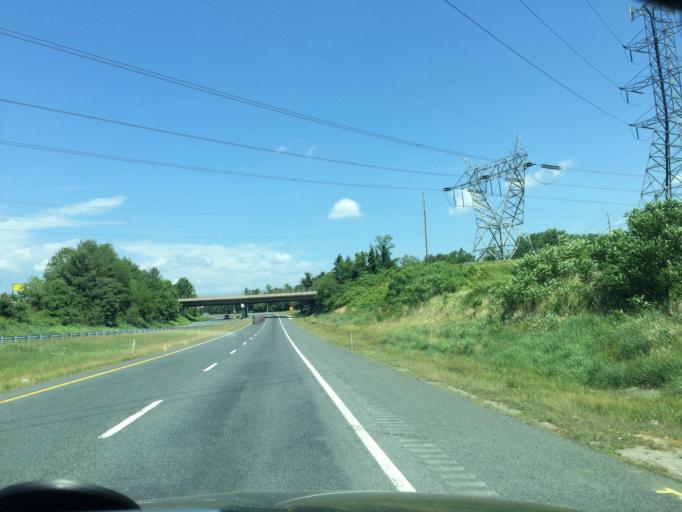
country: US
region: Maryland
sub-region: Baltimore County
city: Reisterstown
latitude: 39.4724
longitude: -76.8377
